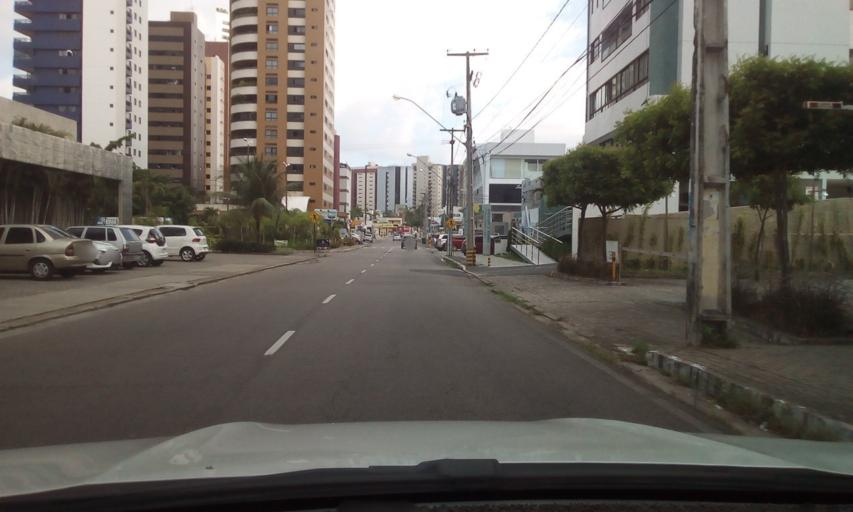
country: BR
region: Paraiba
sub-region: Joao Pessoa
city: Joao Pessoa
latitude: -7.1105
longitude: -34.8295
